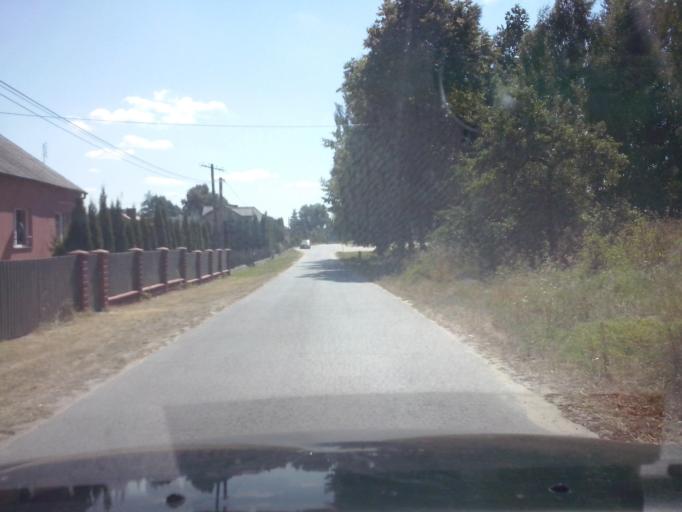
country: PL
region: Swietokrzyskie
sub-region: Powiat buski
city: Gnojno
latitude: 50.6229
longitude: 20.8806
